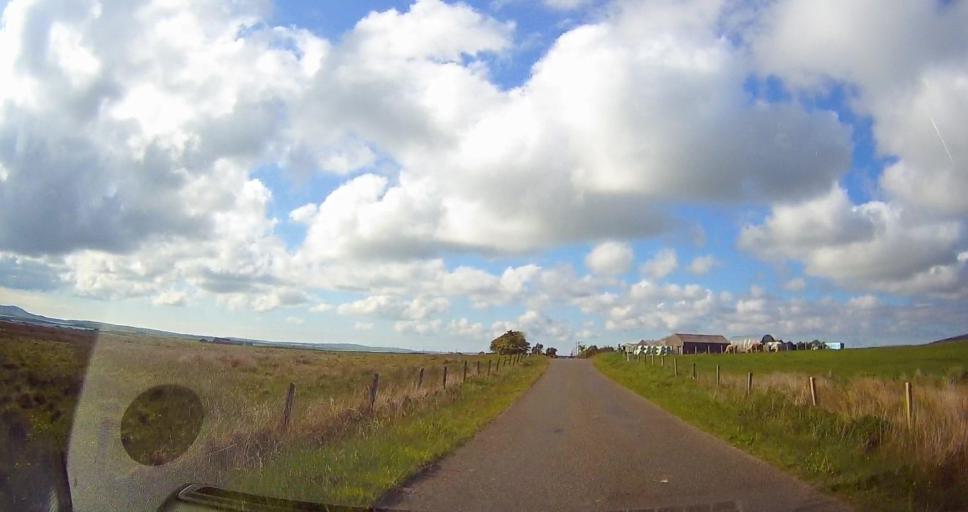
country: GB
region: Scotland
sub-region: Orkney Islands
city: Stromness
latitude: 58.9918
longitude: -3.1567
